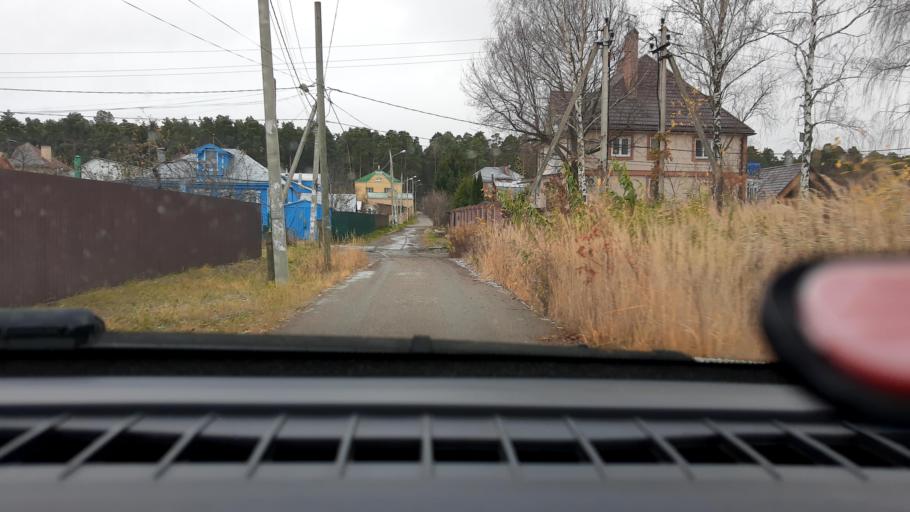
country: RU
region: Nizjnij Novgorod
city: Burevestnik
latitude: 56.2020
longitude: 43.7829
